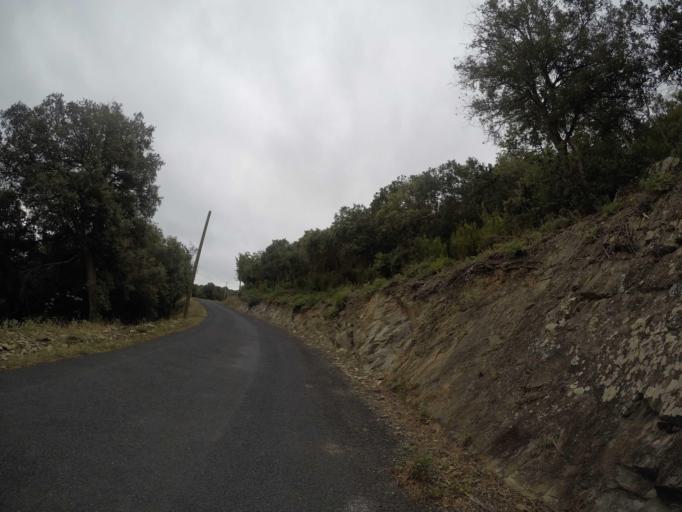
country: FR
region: Languedoc-Roussillon
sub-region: Departement des Pyrenees-Orientales
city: Ille-sur-Tet
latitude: 42.6178
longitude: 2.6195
